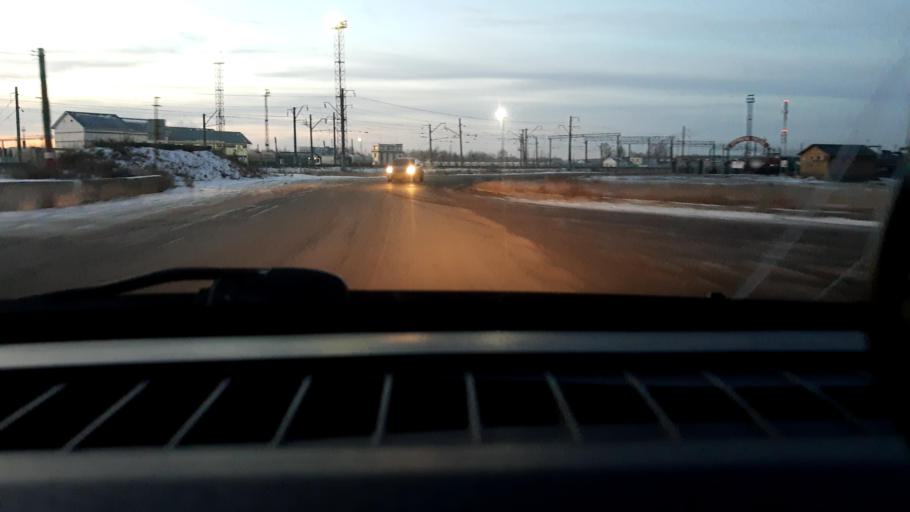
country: RU
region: Nizjnij Novgorod
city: Gorbatovka
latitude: 56.2851
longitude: 43.8478
